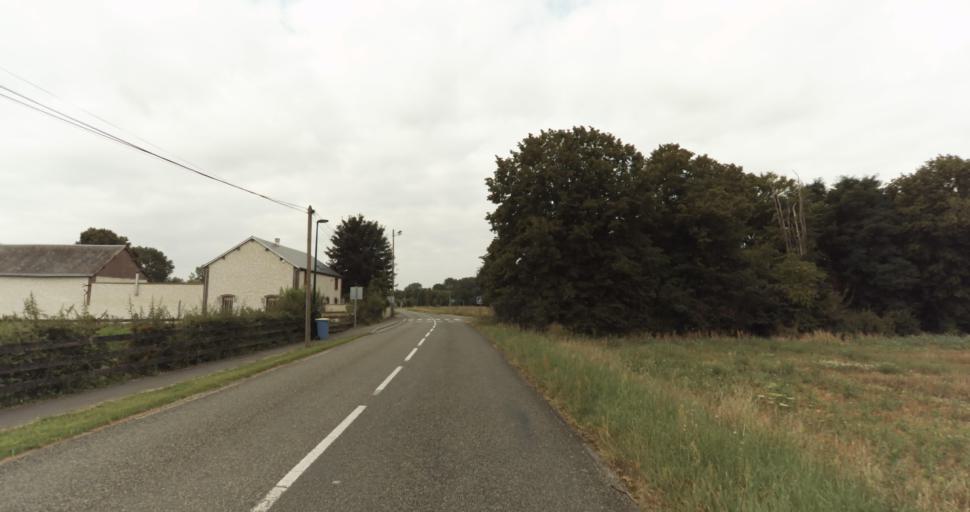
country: FR
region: Centre
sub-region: Departement d'Eure-et-Loir
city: Sorel-Moussel
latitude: 48.8371
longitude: 1.3616
